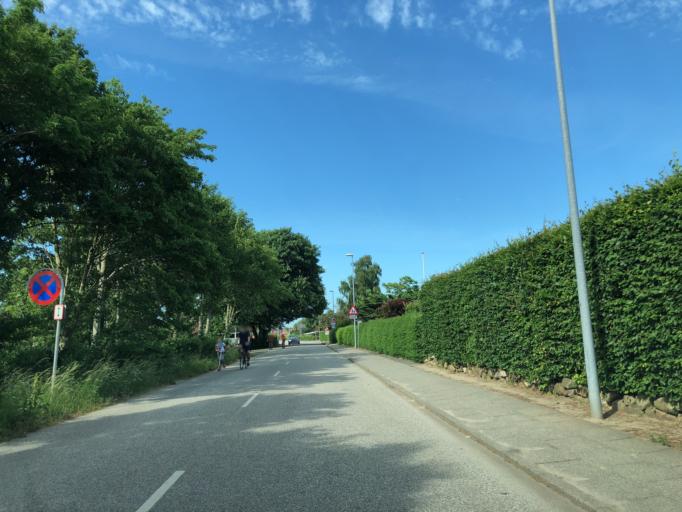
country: DK
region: Central Jutland
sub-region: Herning Kommune
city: Snejbjerg
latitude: 56.1269
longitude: 8.8876
